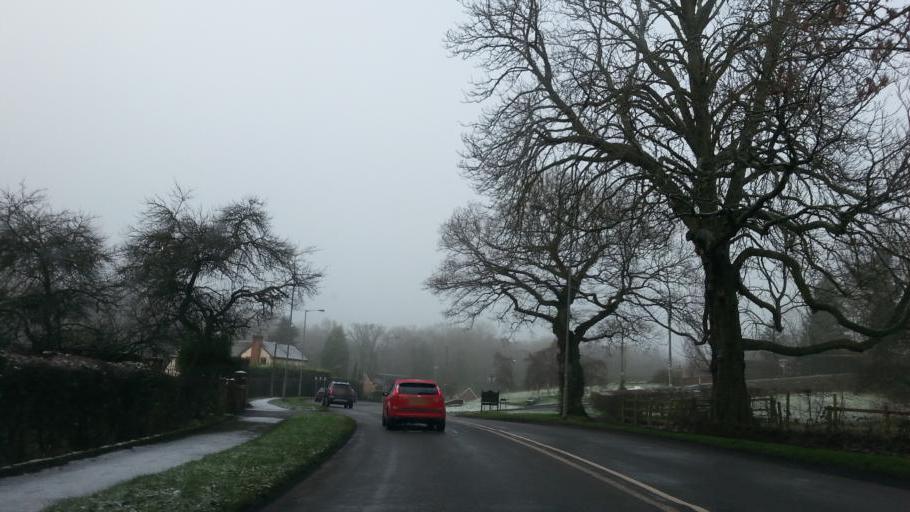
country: GB
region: England
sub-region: Staffordshire
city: Biddulph
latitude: 53.1331
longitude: -2.1665
